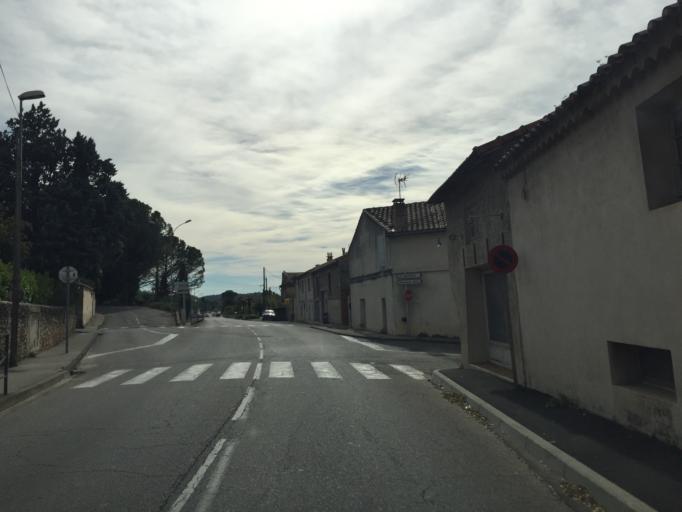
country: FR
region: Provence-Alpes-Cote d'Azur
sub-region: Departement du Vaucluse
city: Bollene
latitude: 44.2770
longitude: 4.7448
